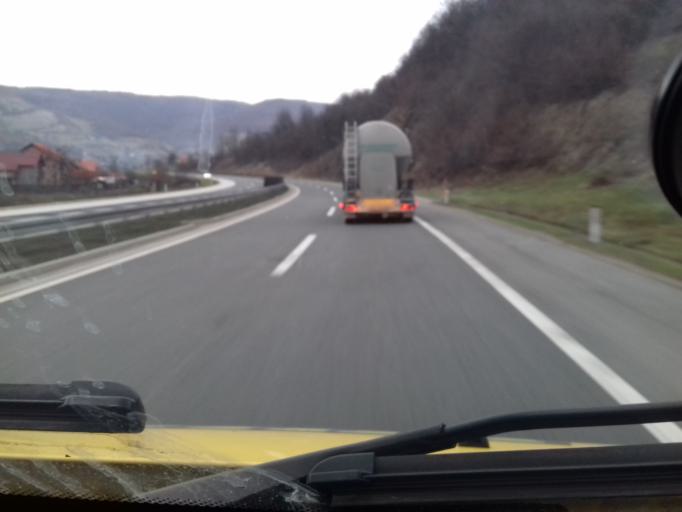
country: BA
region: Federation of Bosnia and Herzegovina
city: Ilijas
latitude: 43.9370
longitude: 18.2788
